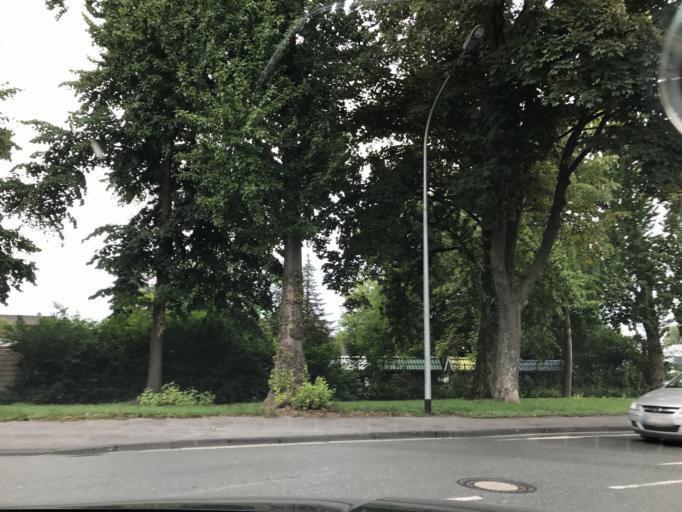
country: DE
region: North Rhine-Westphalia
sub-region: Regierungsbezirk Dusseldorf
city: Essen
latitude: 51.4707
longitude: 6.9615
